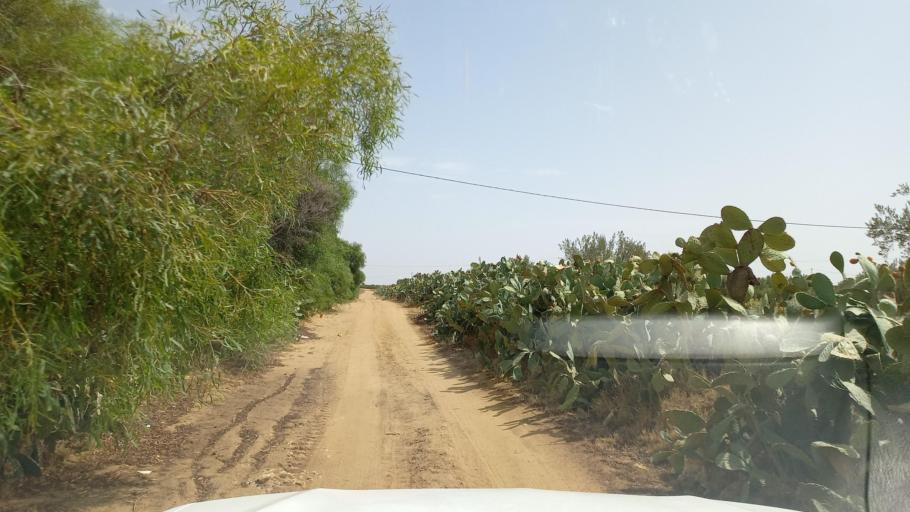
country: TN
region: Al Qasrayn
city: Kasserine
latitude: 35.2431
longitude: 9.0675
